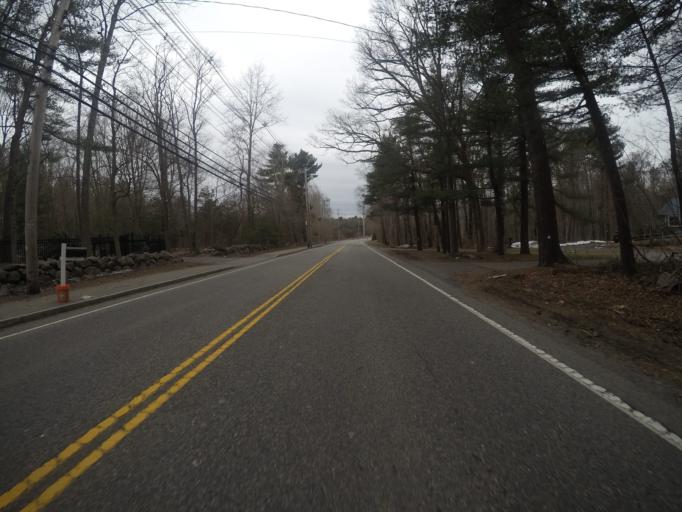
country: US
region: Massachusetts
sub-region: Bristol County
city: Easton
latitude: 42.0313
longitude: -71.1121
